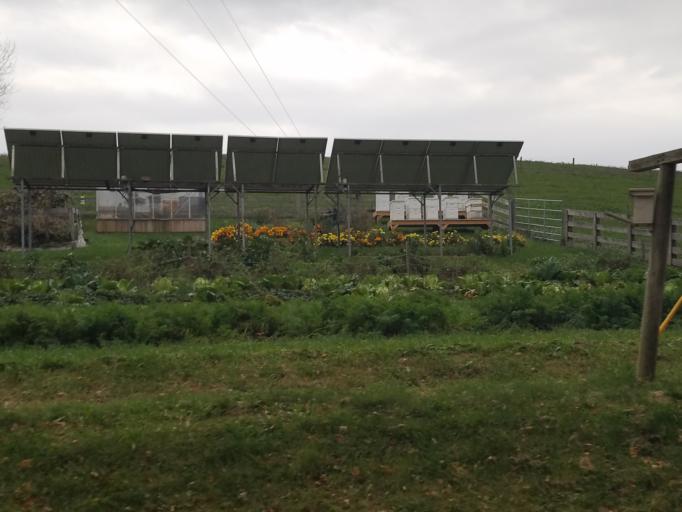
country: US
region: Ohio
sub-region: Knox County
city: Danville
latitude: 40.5380
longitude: -82.3379
